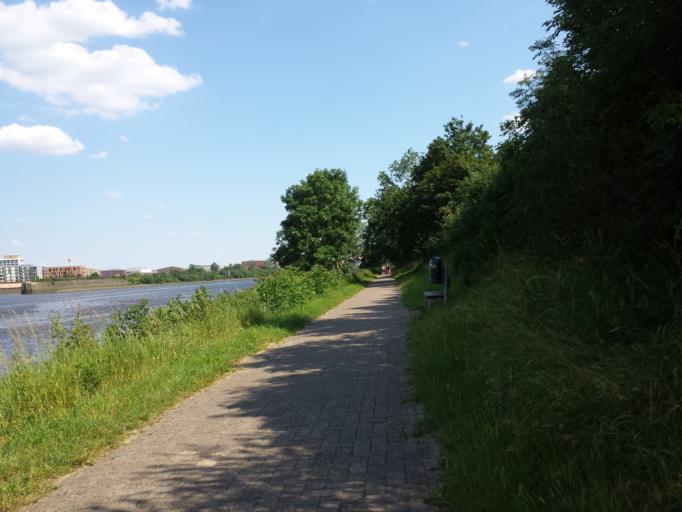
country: DE
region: Bremen
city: Bremen
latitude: 53.0965
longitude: 8.7550
